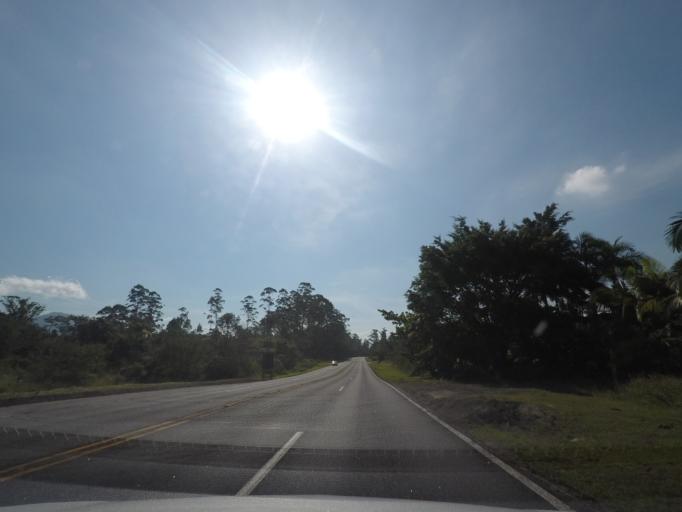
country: BR
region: Parana
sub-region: Pontal Do Parana
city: Pontal do Parana
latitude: -25.6054
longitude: -48.6076
